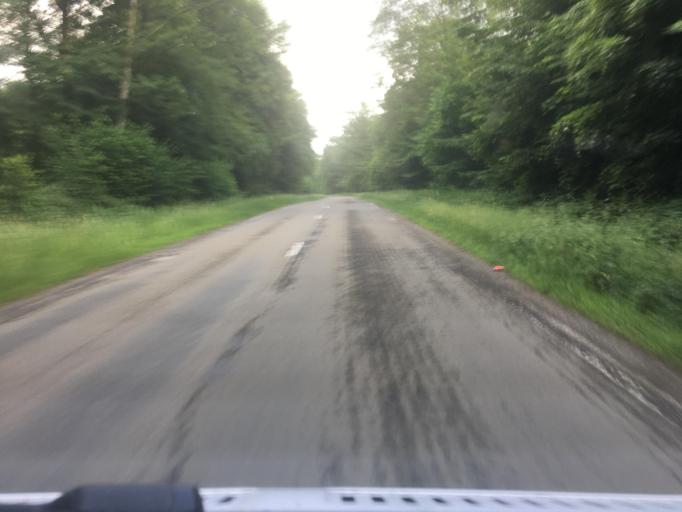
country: BE
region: Wallonia
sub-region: Province du Luxembourg
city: Florenville
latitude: 49.6813
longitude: 5.3340
